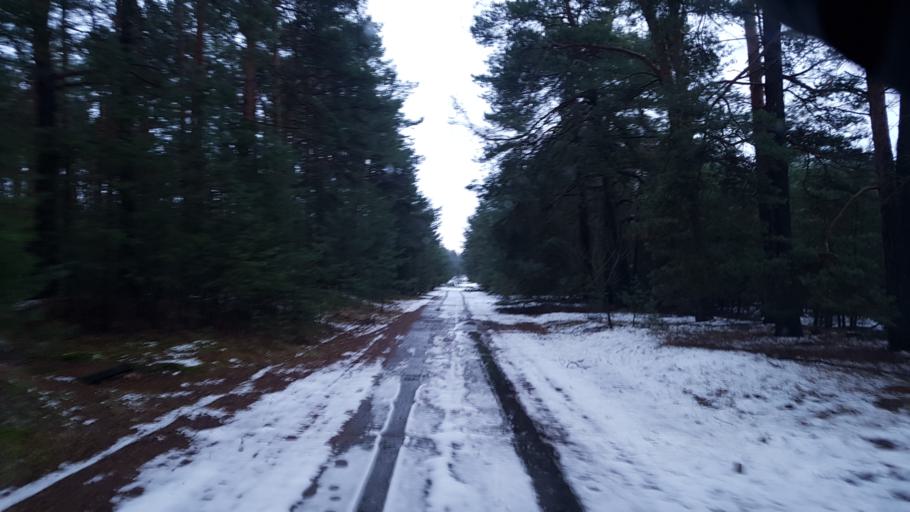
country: DE
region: Brandenburg
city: Janschwalde
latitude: 51.8851
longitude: 14.5464
